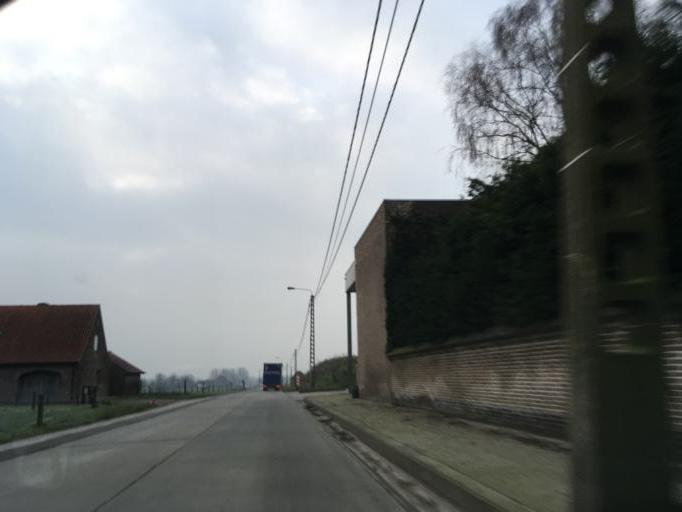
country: BE
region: Flanders
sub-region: Provincie West-Vlaanderen
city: Oostrozebeke
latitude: 50.9439
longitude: 3.3353
